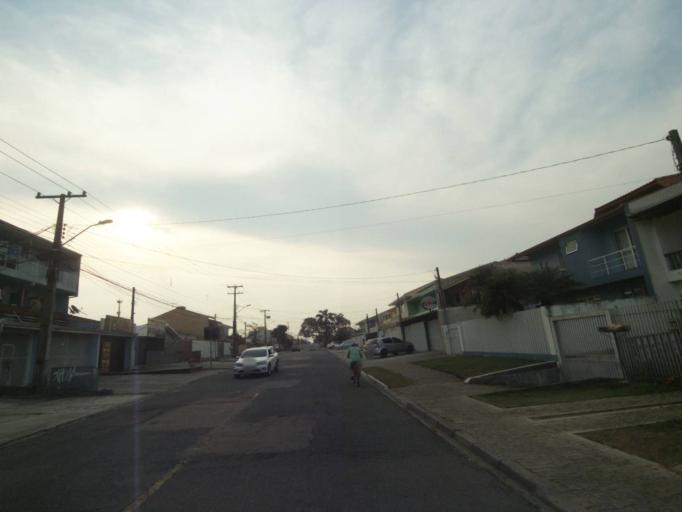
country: BR
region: Parana
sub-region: Sao Jose Dos Pinhais
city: Sao Jose dos Pinhais
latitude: -25.5199
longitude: -49.2748
